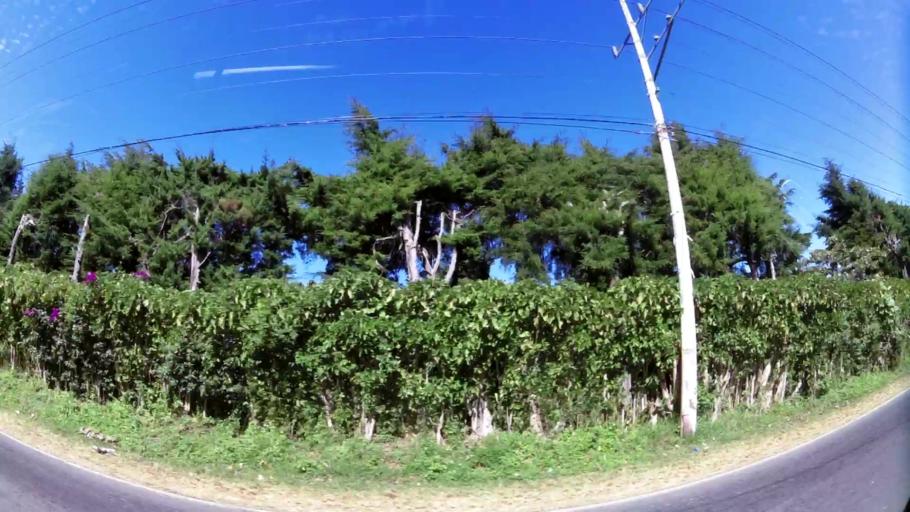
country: SV
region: Ahuachapan
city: Concepcion de Ataco
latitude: 13.8608
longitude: -89.8492
